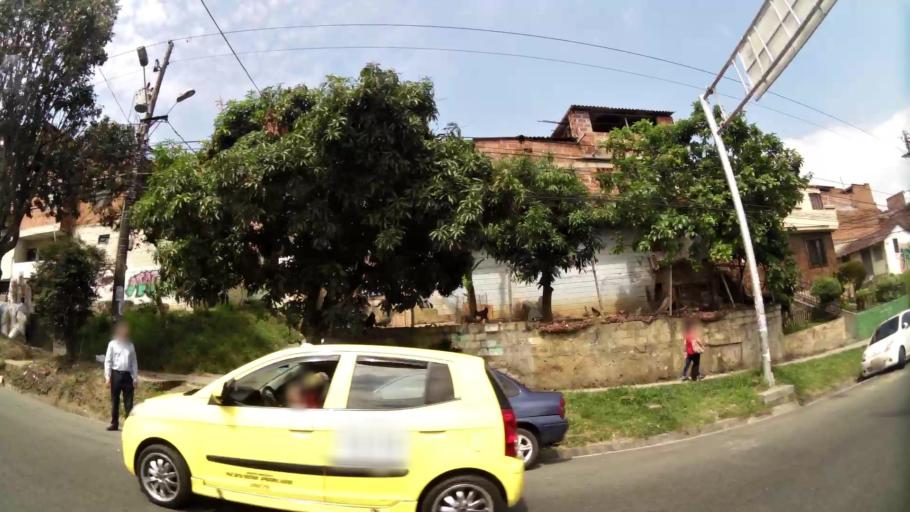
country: CO
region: Antioquia
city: Bello
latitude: 6.3106
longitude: -75.5639
